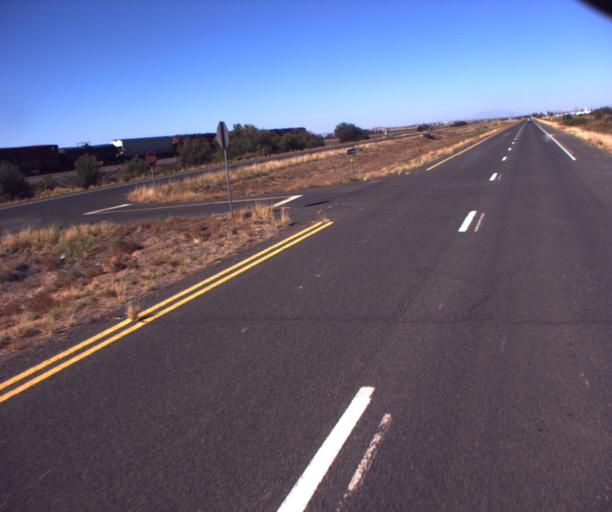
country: US
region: Arizona
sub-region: Navajo County
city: Winslow
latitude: 35.0084
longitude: -110.6616
